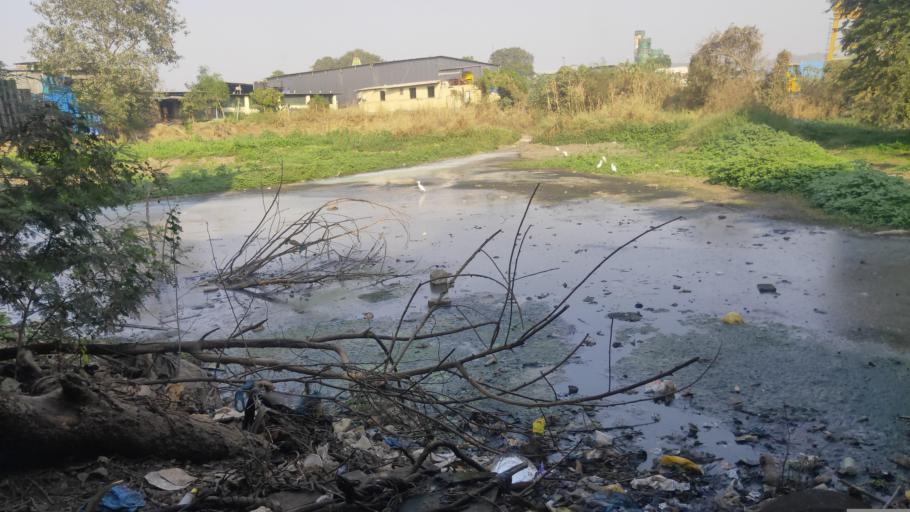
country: IN
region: Maharashtra
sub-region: Thane
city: Bhiwandi
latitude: 19.2530
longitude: 73.0466
